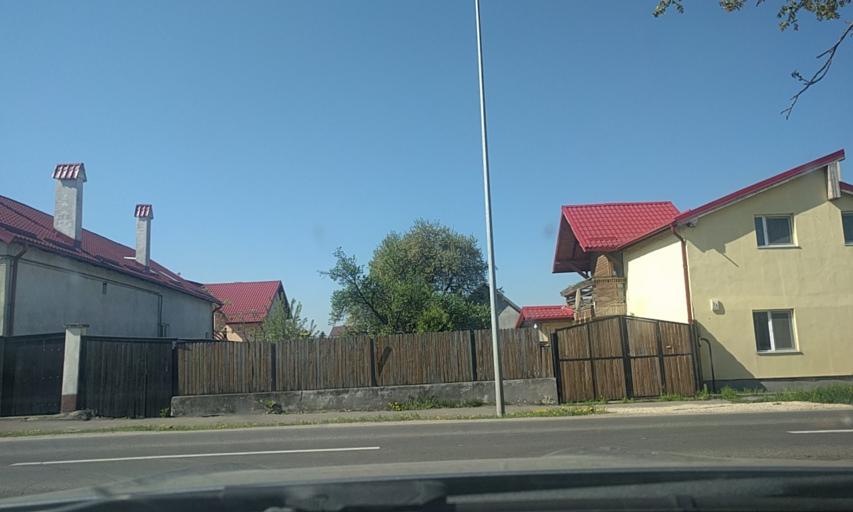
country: RO
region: Brasov
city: Brasov
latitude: 45.6932
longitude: 25.5629
